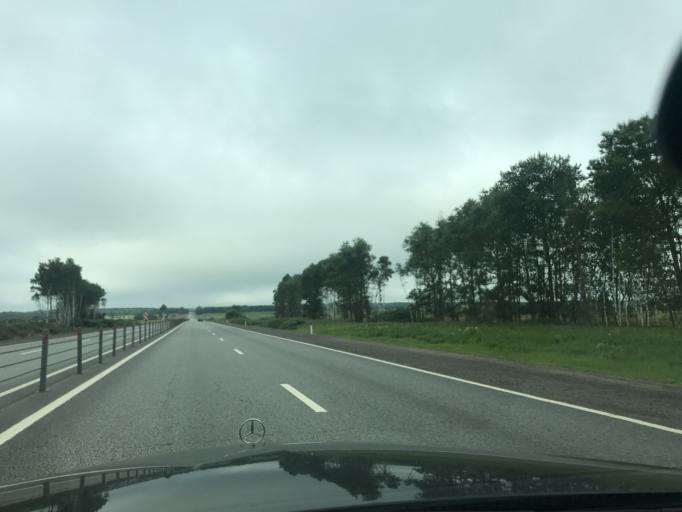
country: RU
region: Smolensk
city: Vyaz'ma
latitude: 55.3435
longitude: 34.6080
